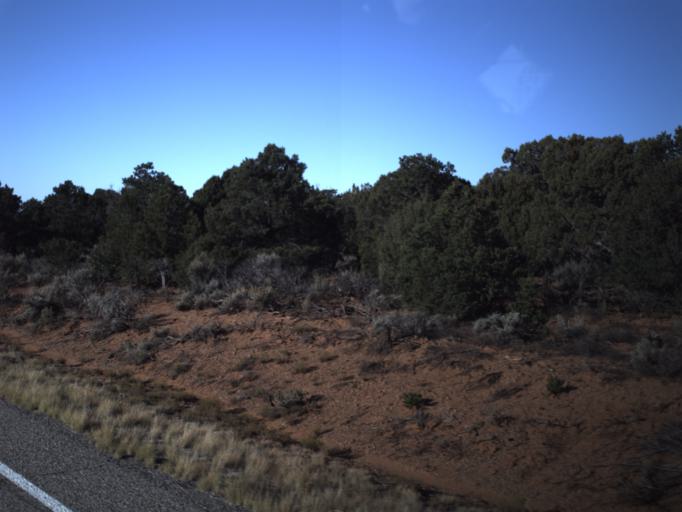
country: US
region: Utah
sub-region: San Juan County
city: Blanding
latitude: 37.5723
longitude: -109.9228
